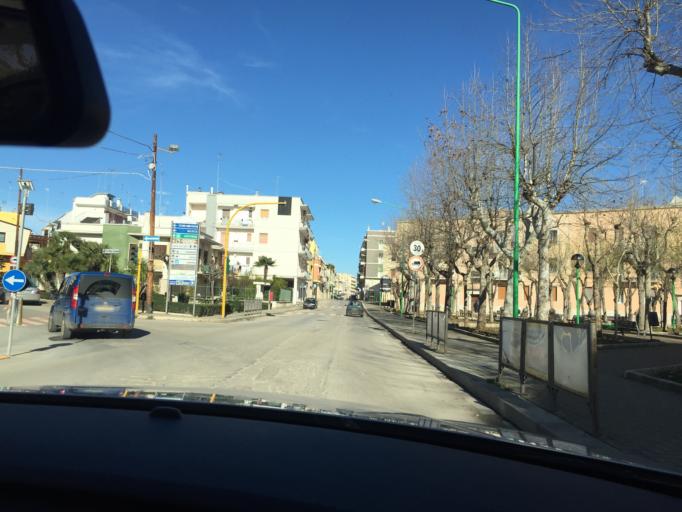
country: IT
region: Apulia
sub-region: Provincia di Bari
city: Terlizzi
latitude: 41.1321
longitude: 16.5344
